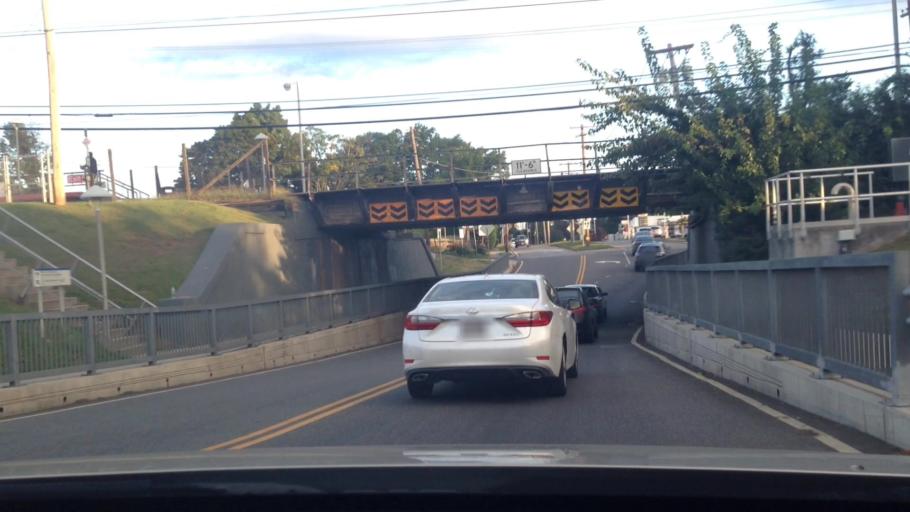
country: US
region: New York
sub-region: Nassau County
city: Garden City Park
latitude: 40.7352
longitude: -73.6608
